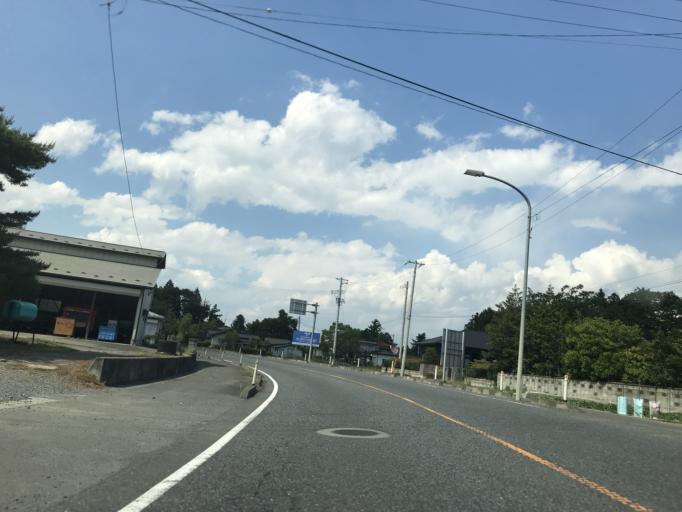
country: JP
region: Miyagi
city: Wakuya
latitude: 38.5004
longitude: 141.1199
